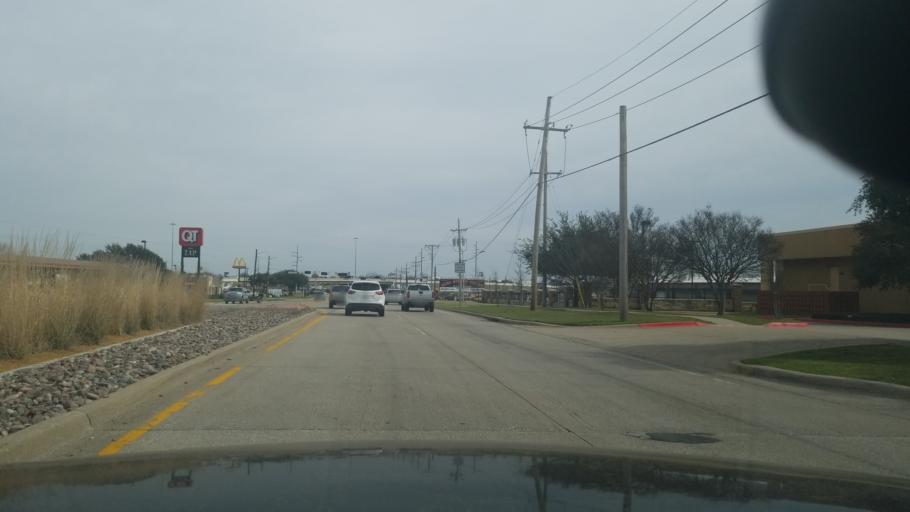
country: US
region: Texas
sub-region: Denton County
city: Highland Village
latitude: 33.0713
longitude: -97.0254
